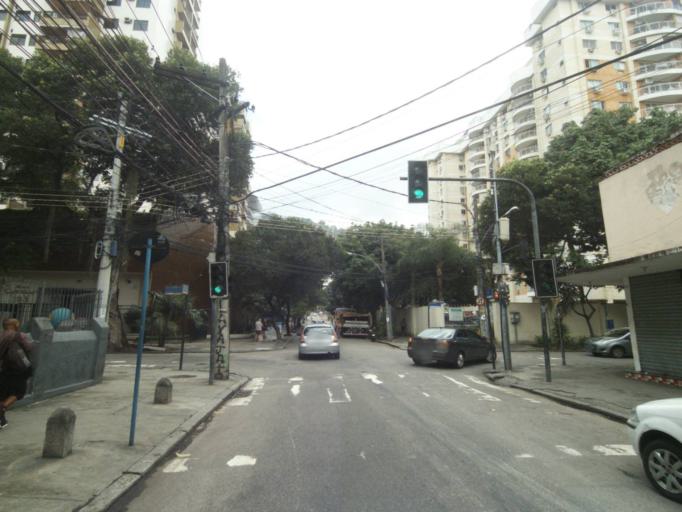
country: BR
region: Rio de Janeiro
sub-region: Rio De Janeiro
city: Rio de Janeiro
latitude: -22.9318
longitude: -43.2465
